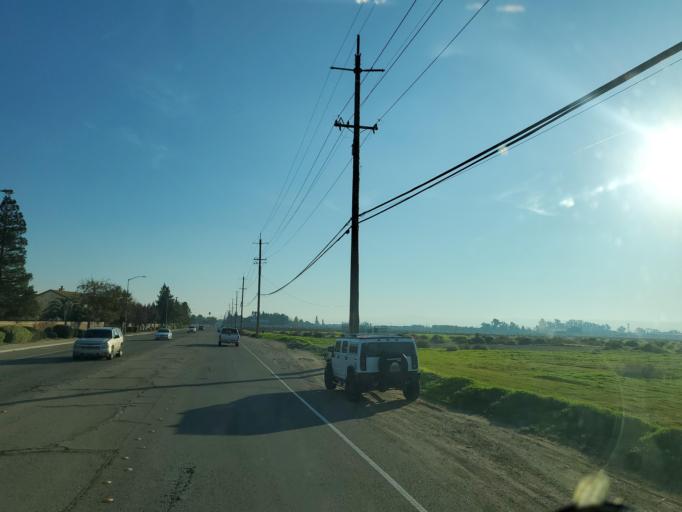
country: US
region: California
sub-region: San Joaquin County
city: Lathrop
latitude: 37.8080
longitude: -121.2528
